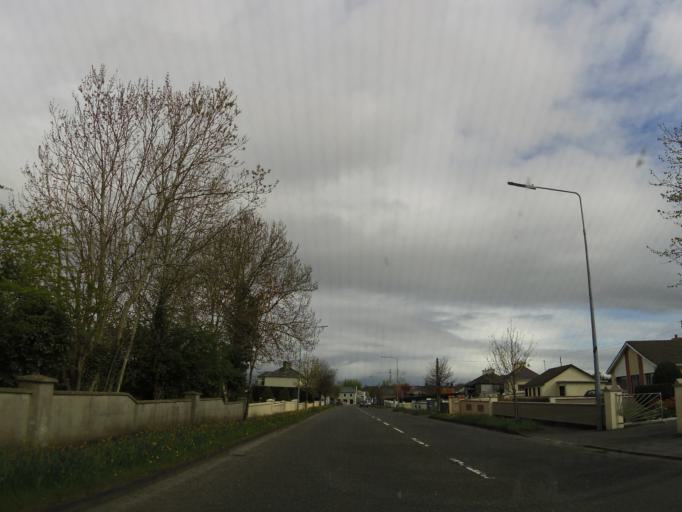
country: IE
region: Connaught
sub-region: Sligo
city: Tobercurry
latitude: 53.9617
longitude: -8.7933
